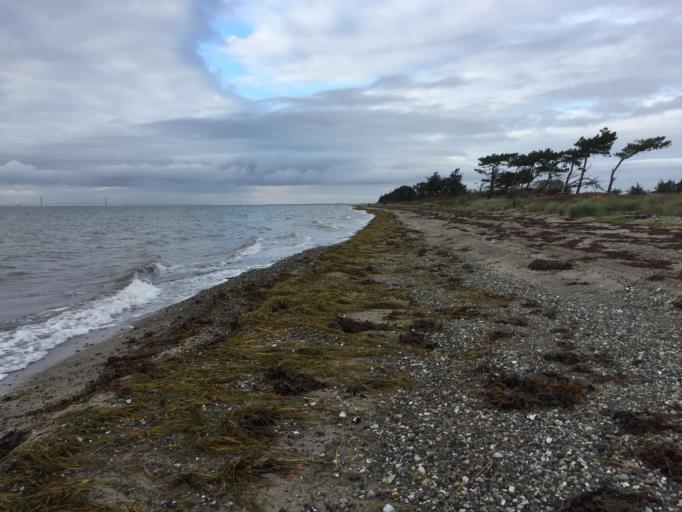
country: DK
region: Zealand
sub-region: Slagelse Kommune
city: Korsor
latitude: 55.2086
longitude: 11.1730
